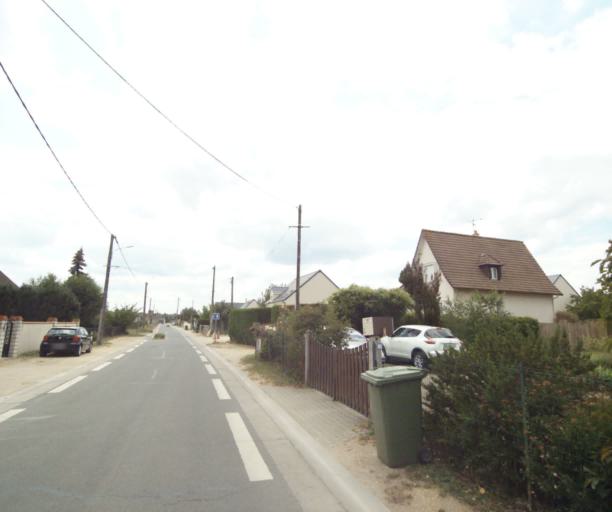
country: FR
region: Centre
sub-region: Departement du Loiret
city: Saint-Hilaire-Saint-Mesmin
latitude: 47.8605
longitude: 1.8470
